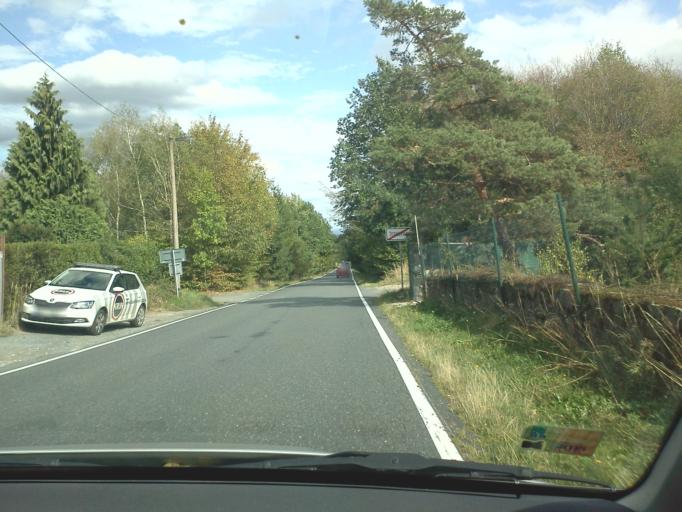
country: CZ
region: Central Bohemia
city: Mukarov
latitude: 50.0009
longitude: 14.7597
